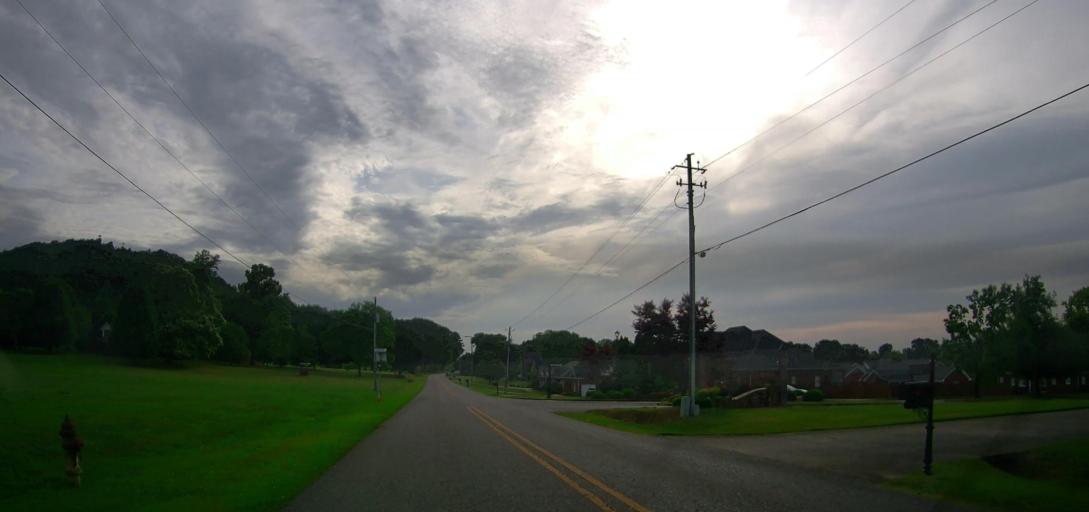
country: US
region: Alabama
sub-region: Calhoun County
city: Oxford
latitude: 33.5763
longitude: -85.8388
